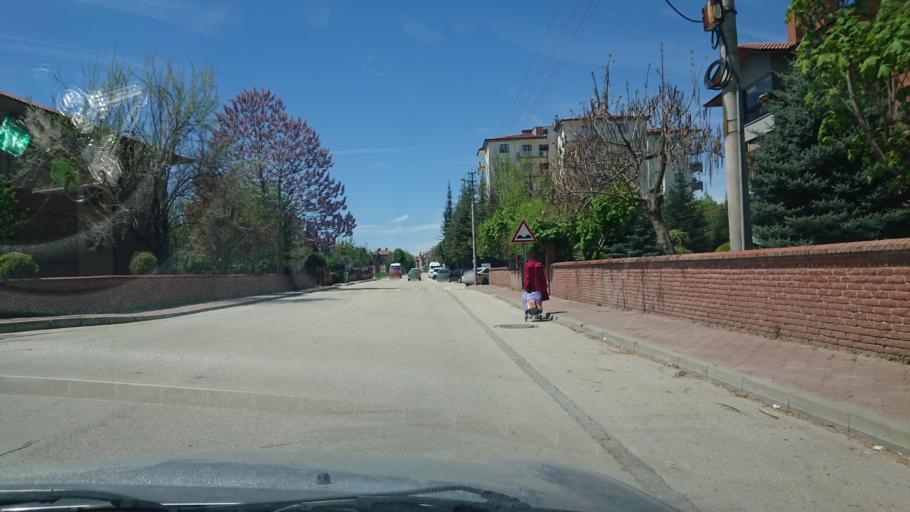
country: TR
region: Eskisehir
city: Eskisehir
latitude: 39.7658
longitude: 30.4939
